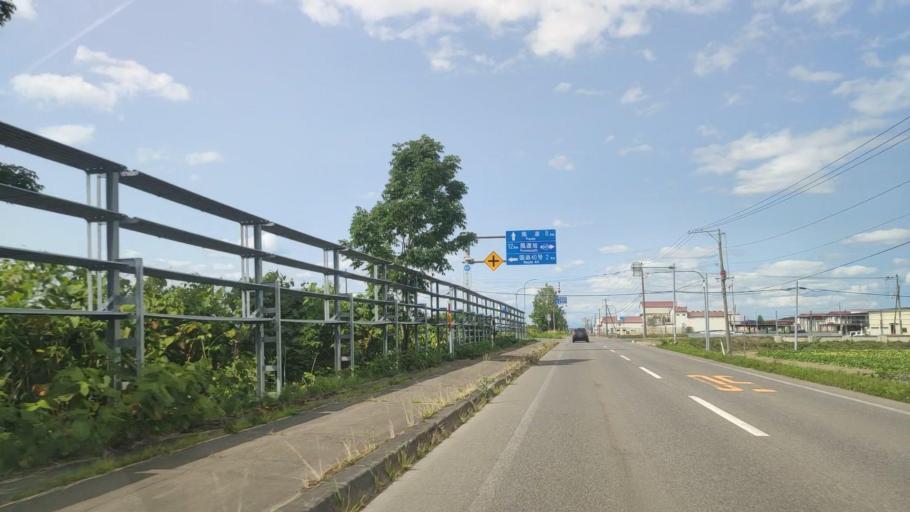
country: JP
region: Hokkaido
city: Nayoro
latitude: 44.2000
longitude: 142.4158
